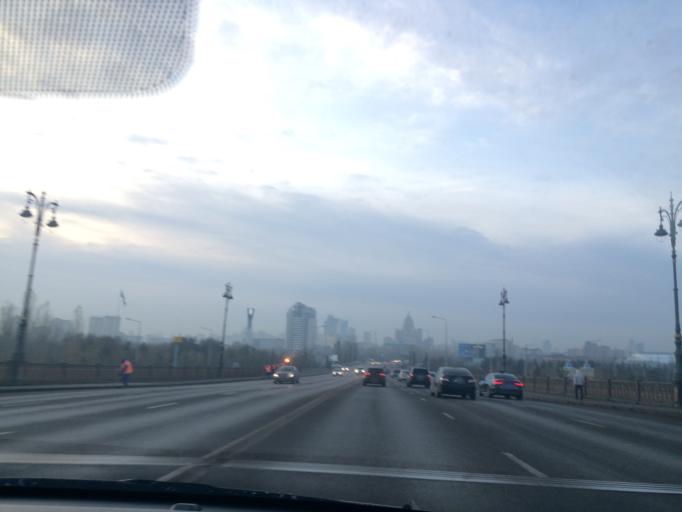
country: KZ
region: Astana Qalasy
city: Astana
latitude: 51.1569
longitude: 71.4115
